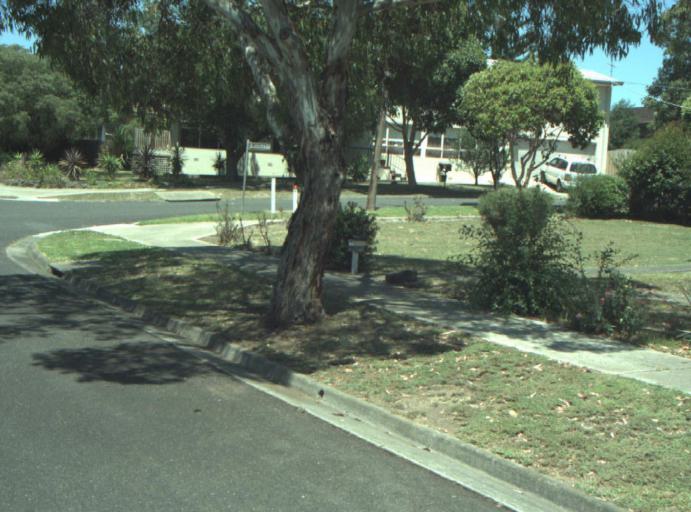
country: AU
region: Victoria
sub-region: Greater Geelong
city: Wandana Heights
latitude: -38.1689
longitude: 144.3166
